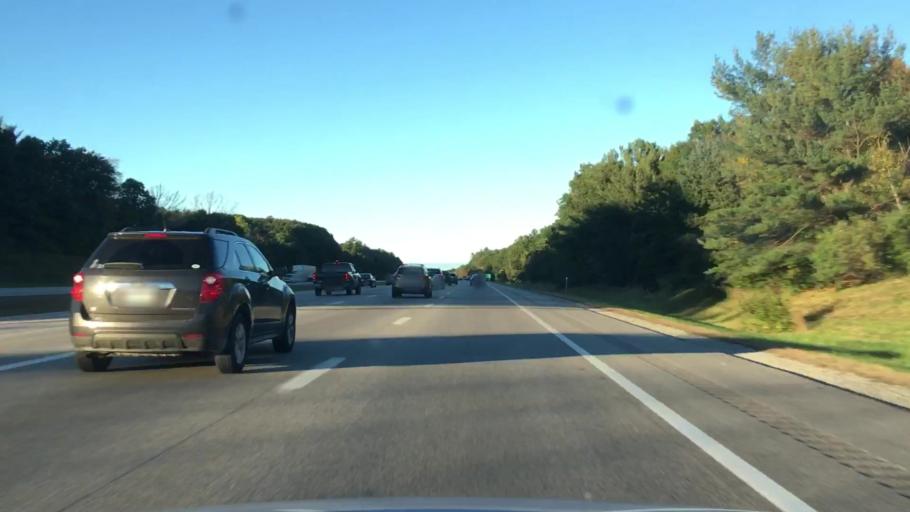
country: US
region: New Hampshire
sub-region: Rockingham County
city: Greenland
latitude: 43.0210
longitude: -70.8297
